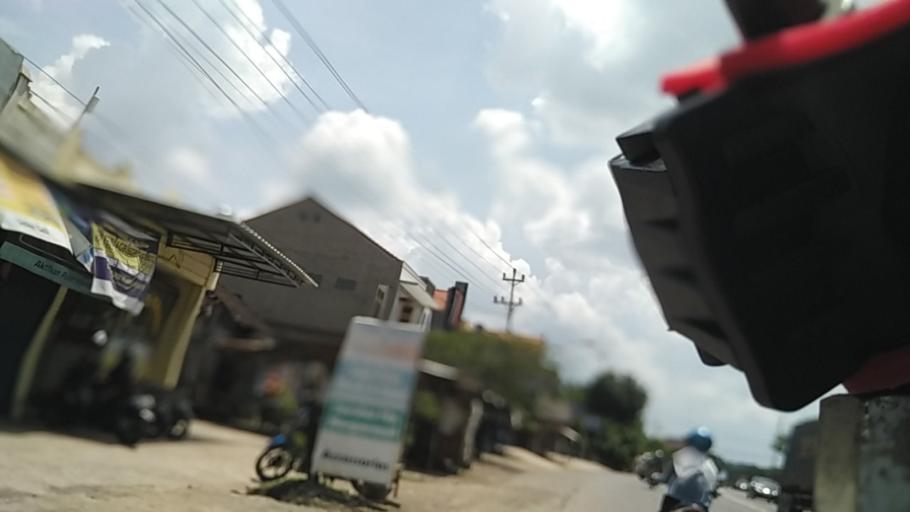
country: ID
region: Central Java
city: Semarang
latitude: -7.0196
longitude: 110.3372
